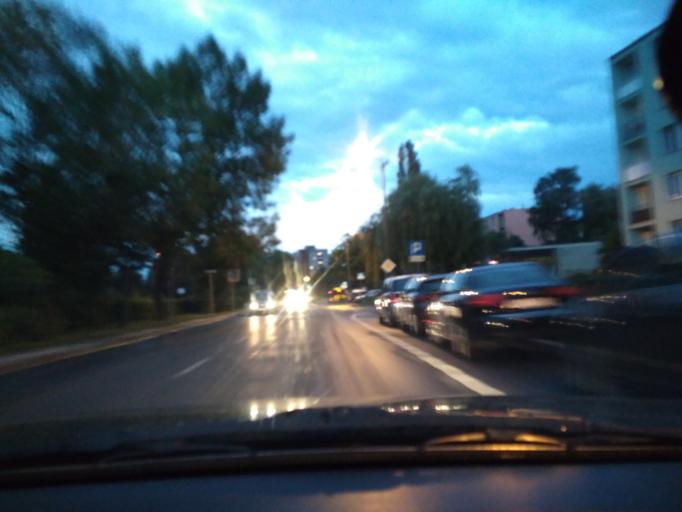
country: PL
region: Silesian Voivodeship
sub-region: Gliwice
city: Gliwice
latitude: 50.2798
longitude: 18.6582
